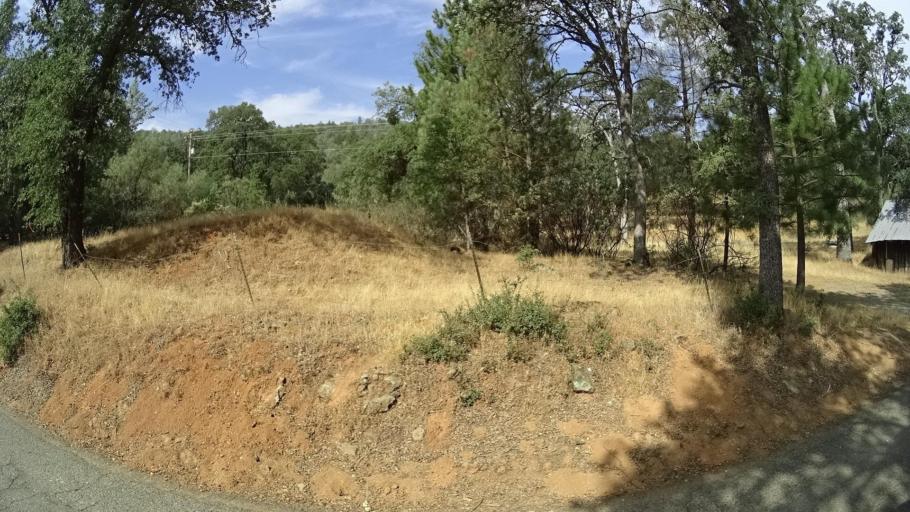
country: US
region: California
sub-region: Mariposa County
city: Mariposa
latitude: 37.5436
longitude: -119.9938
